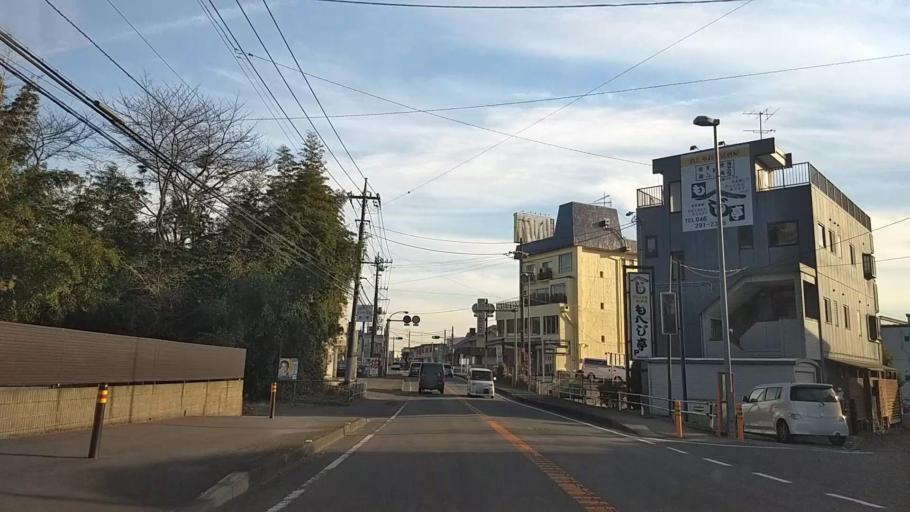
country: JP
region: Kanagawa
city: Atsugi
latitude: 35.4956
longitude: 139.3163
